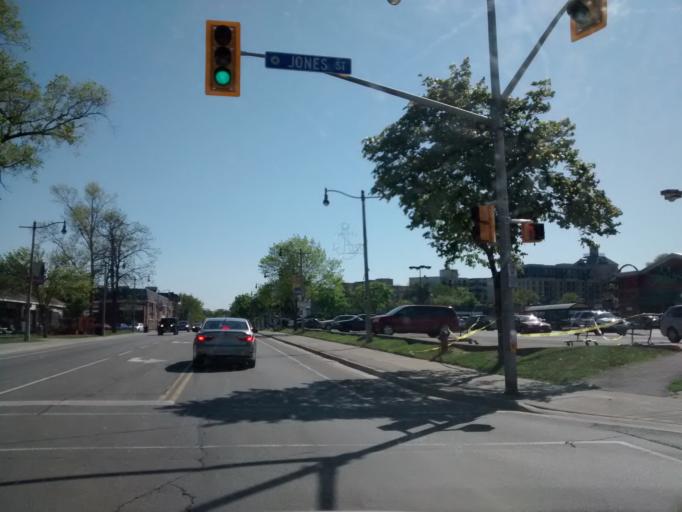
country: CA
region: Ontario
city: Oakville
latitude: 43.3958
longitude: -79.7103
